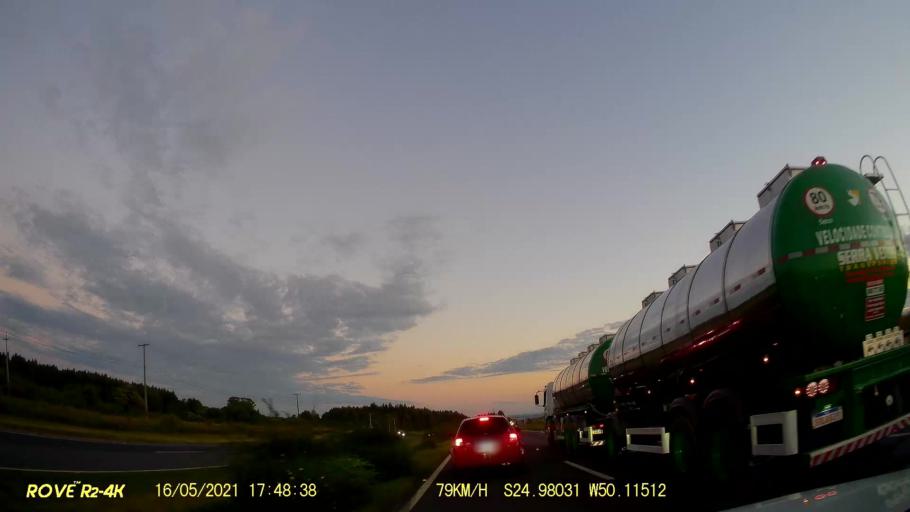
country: BR
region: Parana
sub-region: Carambei
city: Carambei
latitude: -24.9800
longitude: -50.1166
